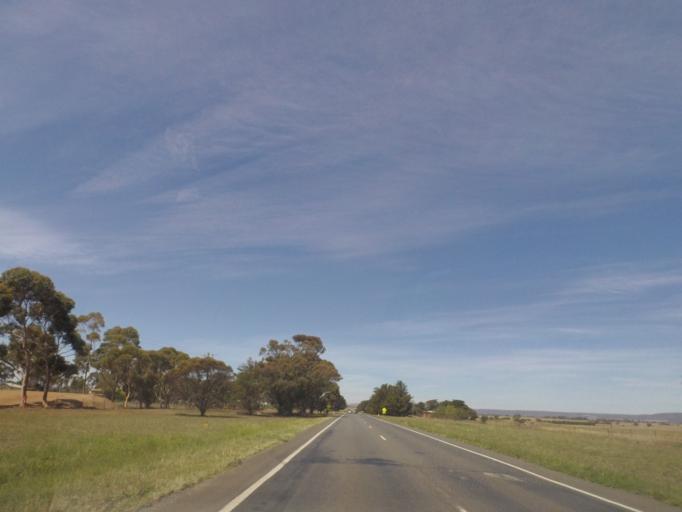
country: AU
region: Victoria
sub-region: Moorabool
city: Bacchus Marsh
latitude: -37.7928
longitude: 144.4166
